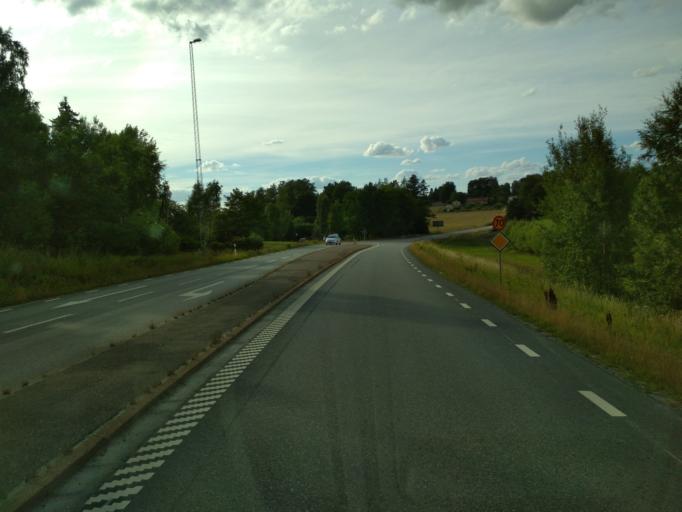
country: SE
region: Uppsala
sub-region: Habo Kommun
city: Balsta
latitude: 59.6258
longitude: 17.4920
